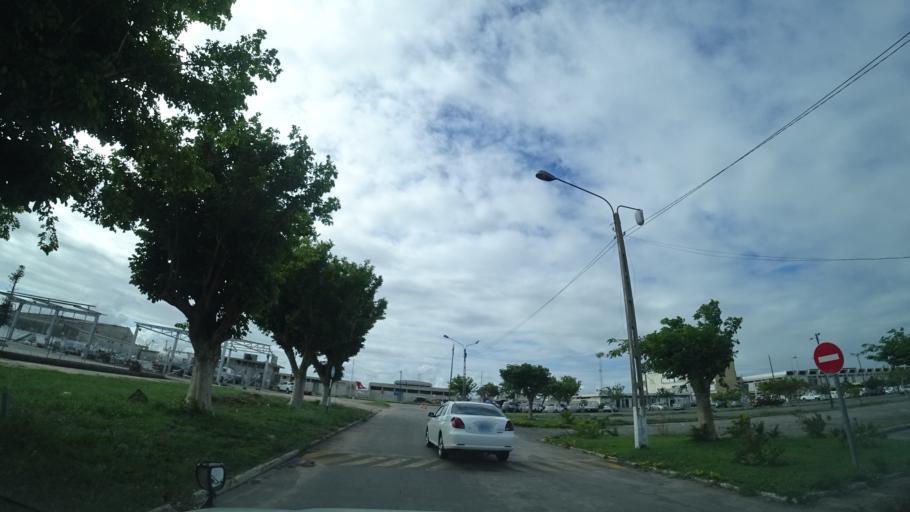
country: MZ
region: Sofala
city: Beira
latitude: -19.7991
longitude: 34.9003
